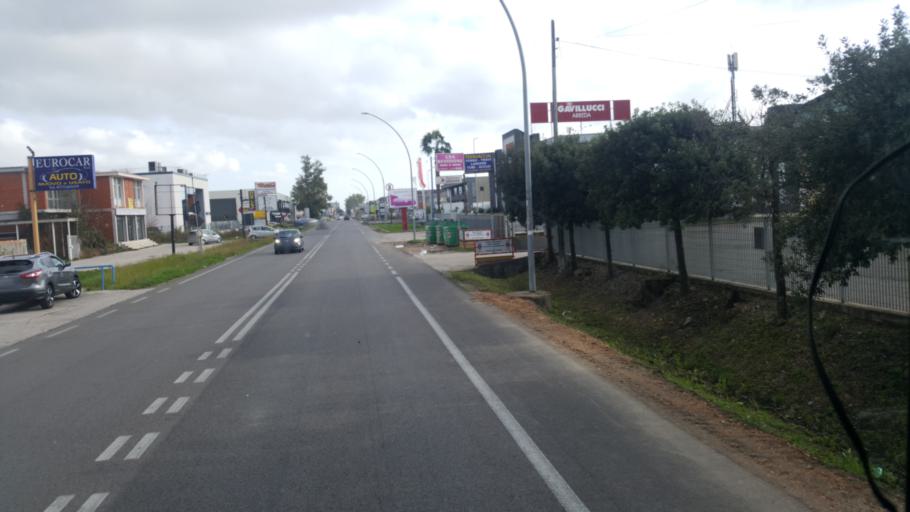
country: IT
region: Latium
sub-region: Provincia di Latina
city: Latina
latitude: 41.4773
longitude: 12.8762
